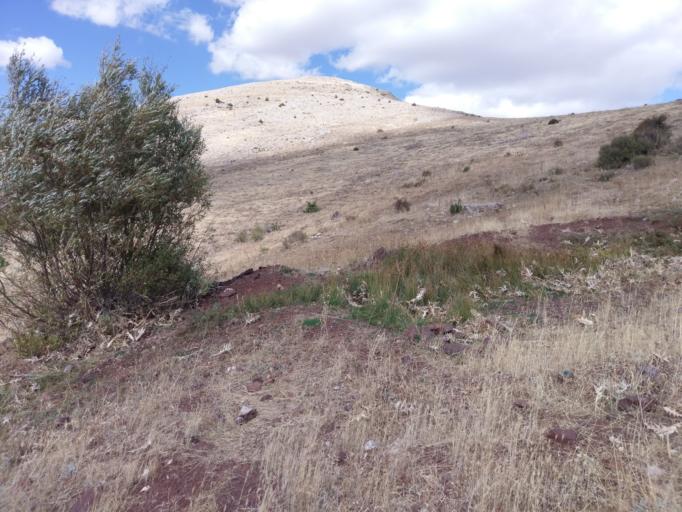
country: TR
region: Kayseri
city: Toklar
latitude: 38.4112
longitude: 36.1094
